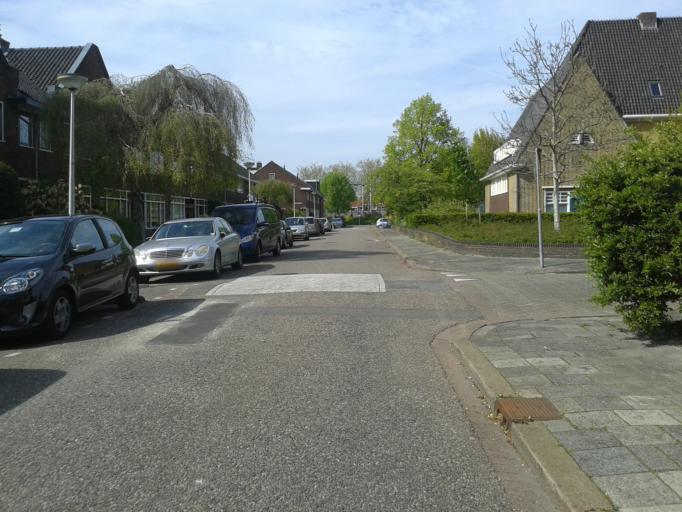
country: NL
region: South Holland
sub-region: Gemeente Gouda
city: Gouda
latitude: 52.0154
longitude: 4.7154
